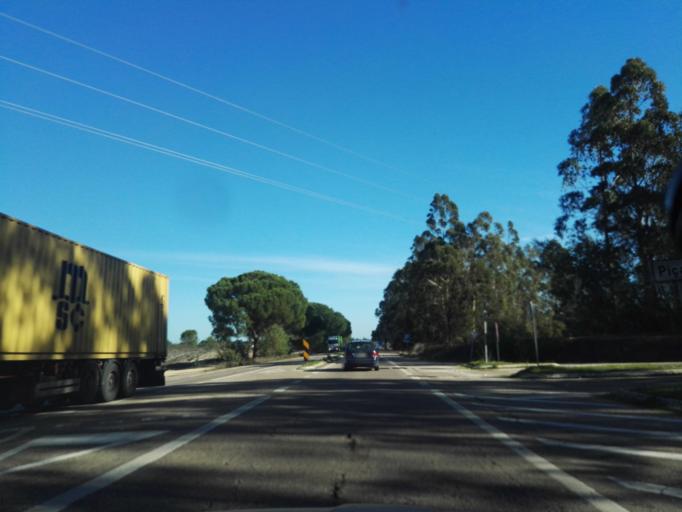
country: PT
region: Evora
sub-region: Vendas Novas
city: Vendas Novas
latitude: 38.6810
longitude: -8.5560
